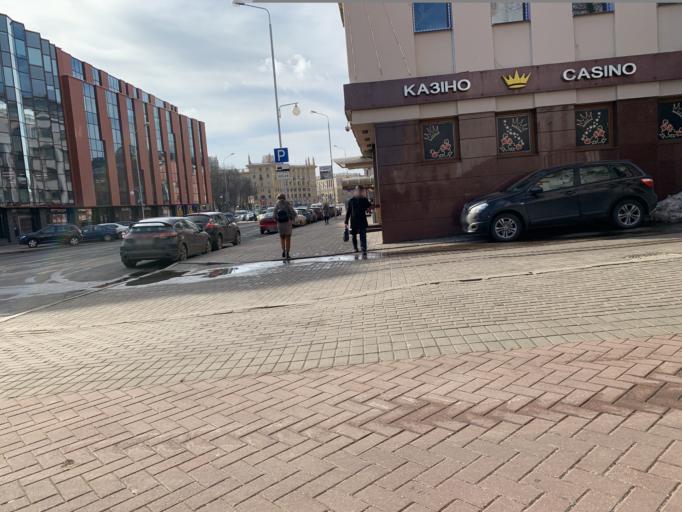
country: BY
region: Minsk
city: Minsk
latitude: 53.8956
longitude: 27.5560
